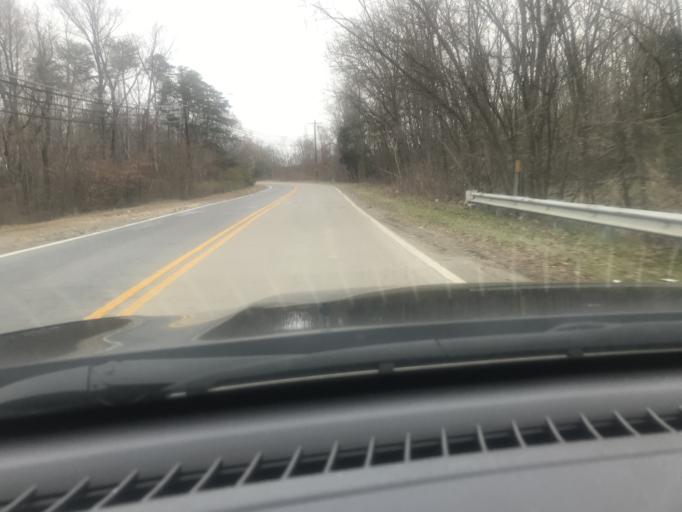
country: US
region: Maryland
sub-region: Prince George's County
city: Friendly
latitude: 38.7737
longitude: -76.9692
